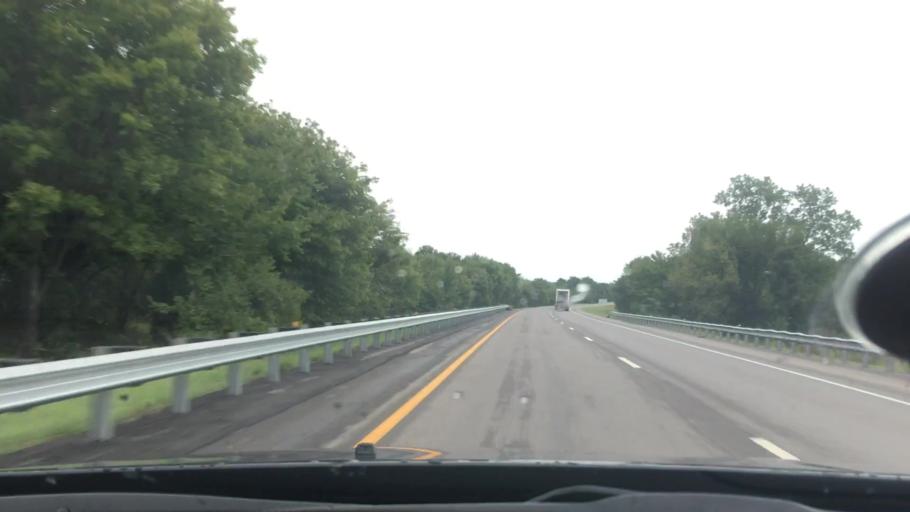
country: US
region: Oklahoma
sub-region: Okmulgee County
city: Morris
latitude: 35.4455
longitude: -95.7686
